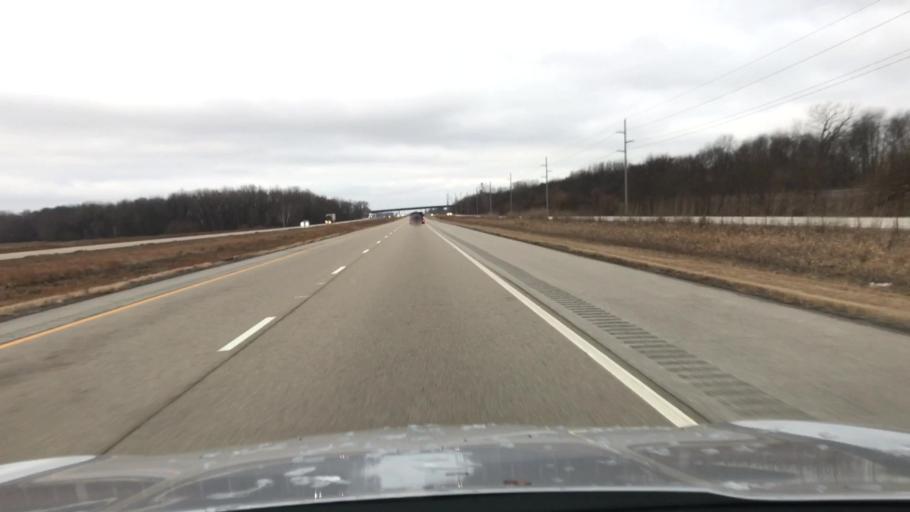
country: US
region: Illinois
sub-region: Logan County
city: Atlanta
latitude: 40.2272
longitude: -89.2708
